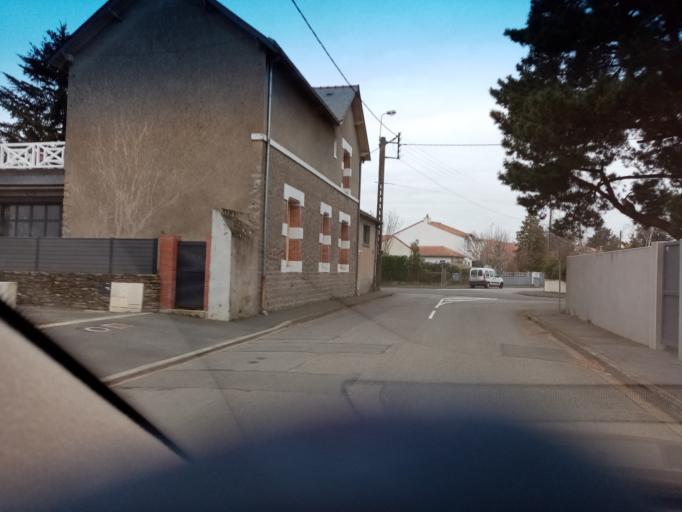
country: FR
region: Pays de la Loire
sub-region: Departement de la Loire-Atlantique
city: Saint-Sebastien-sur-Loire
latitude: 47.2021
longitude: -1.5107
